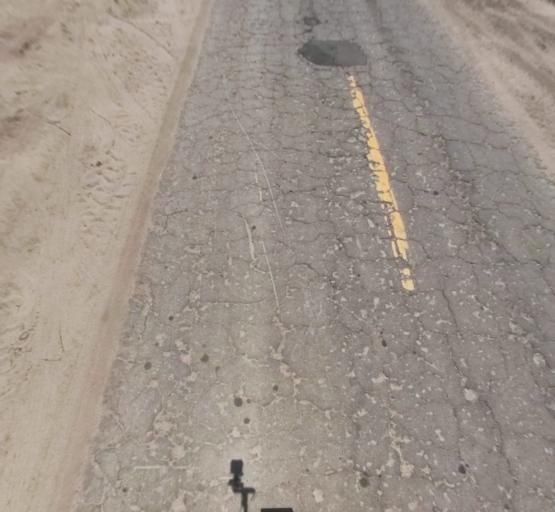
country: US
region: California
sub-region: Fresno County
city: Biola
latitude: 36.8329
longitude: -120.1330
